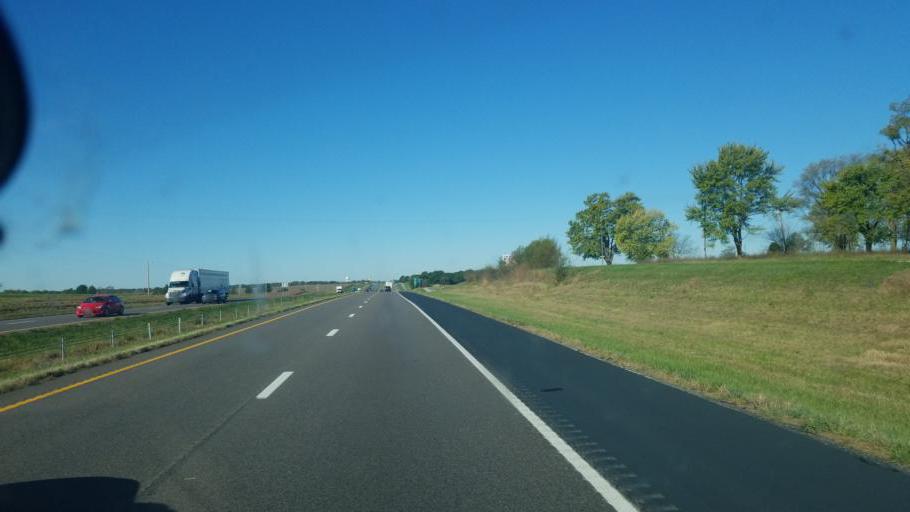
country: US
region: Missouri
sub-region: Callaway County
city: Fulton
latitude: 38.9439
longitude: -91.8995
